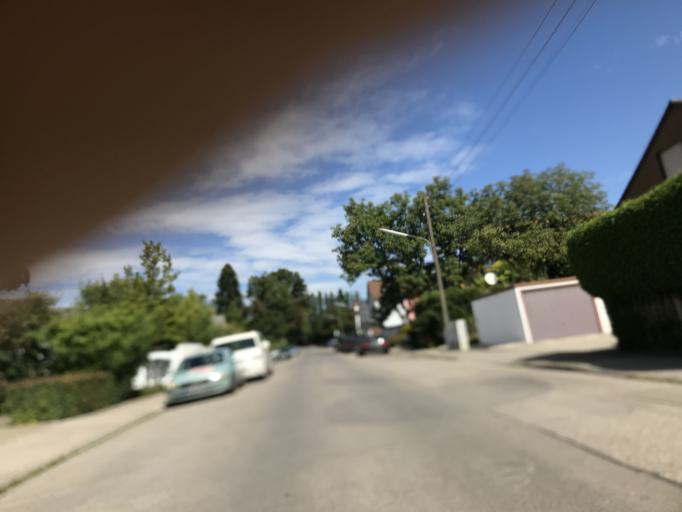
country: DE
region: Bavaria
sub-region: Upper Bavaria
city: Grobenzell
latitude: 48.1925
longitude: 11.3663
